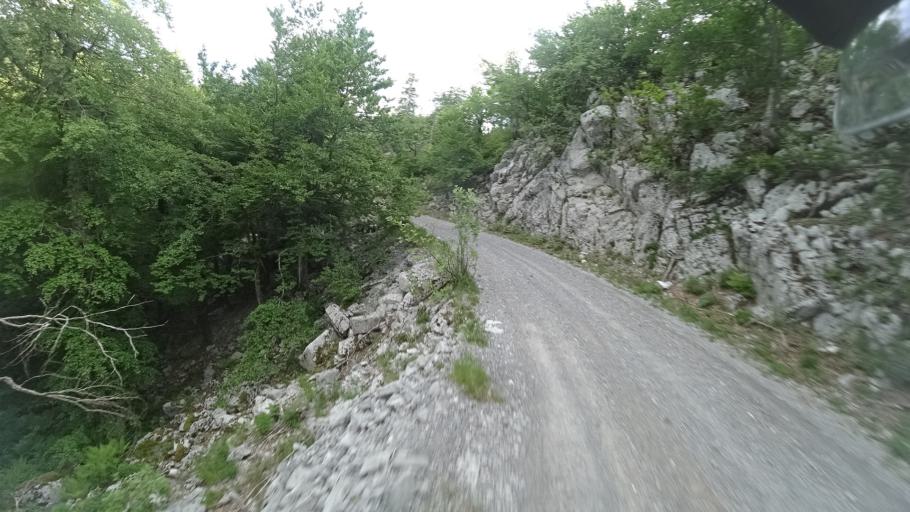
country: HR
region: Licko-Senjska
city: Gospic
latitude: 44.4585
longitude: 15.3005
